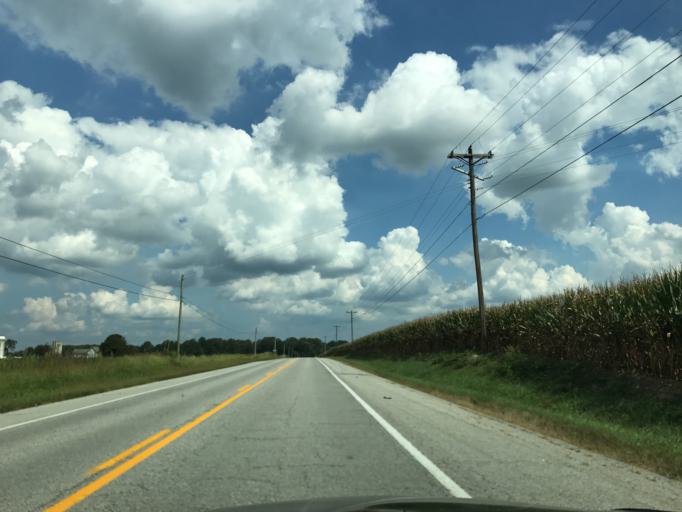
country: US
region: Maryland
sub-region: Queen Anne's County
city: Kingstown
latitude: 39.1799
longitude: -75.9044
